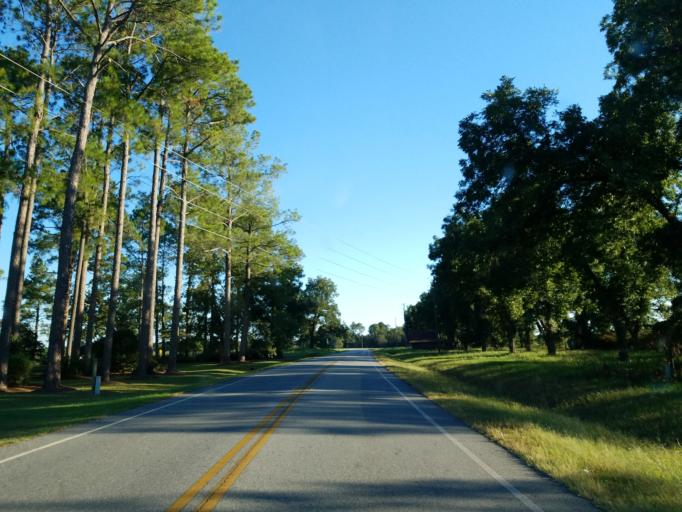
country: US
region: Georgia
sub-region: Worth County
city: Sylvester
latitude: 31.6794
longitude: -83.8780
